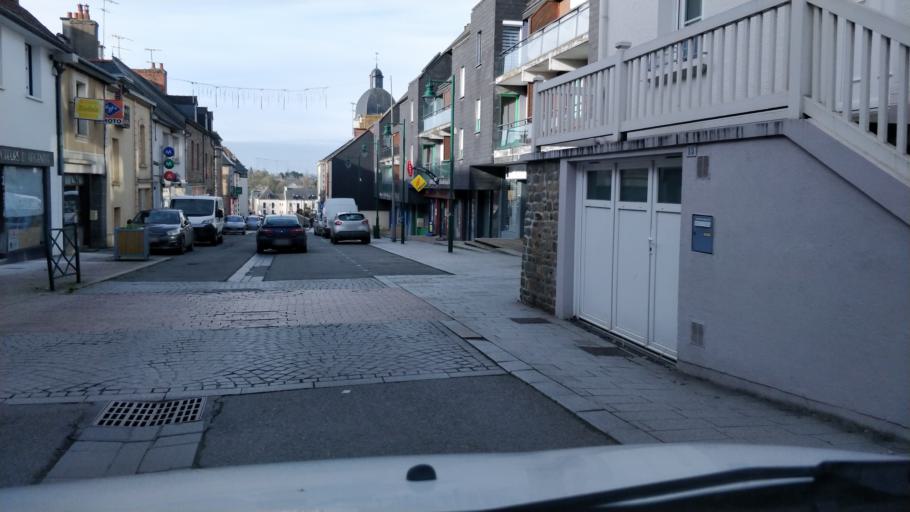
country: FR
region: Brittany
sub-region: Departement d'Ille-et-Vilaine
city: Argentre-du-Plessis
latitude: 48.0570
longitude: -1.1494
